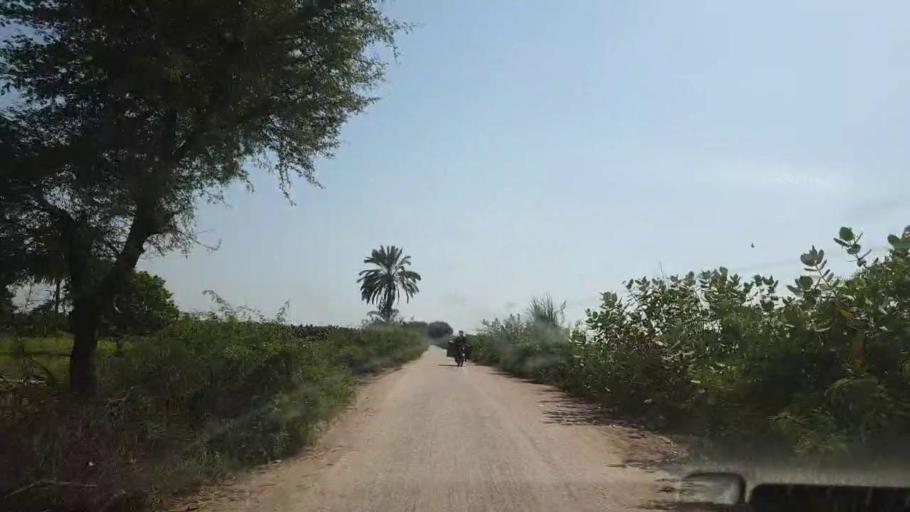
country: PK
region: Sindh
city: Tando Jam
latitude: 25.3987
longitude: 68.5870
